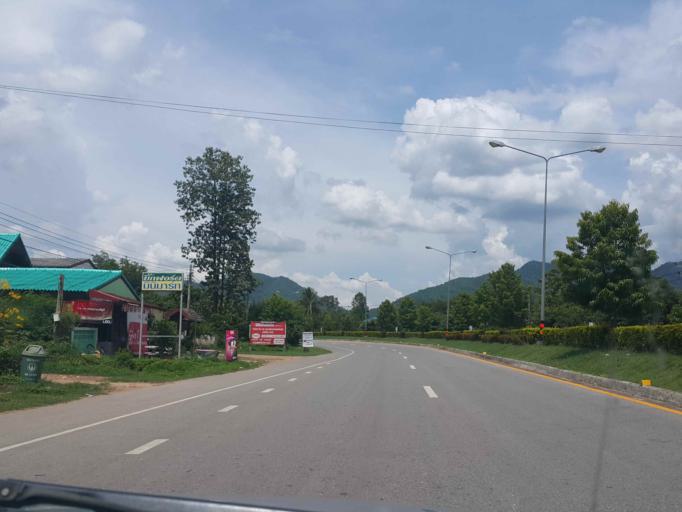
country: TH
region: Nan
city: Ban Luang
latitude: 18.8497
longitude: 100.4423
